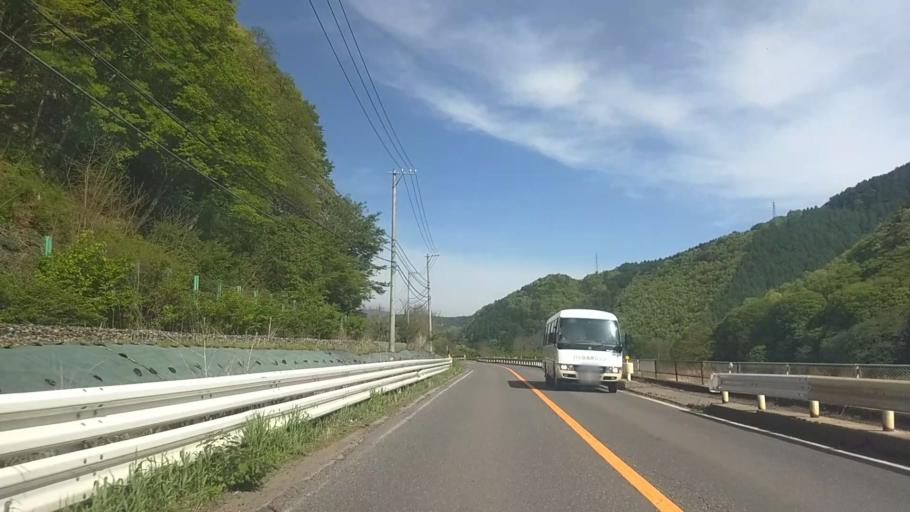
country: JP
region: Nagano
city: Saku
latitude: 36.0323
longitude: 138.4842
